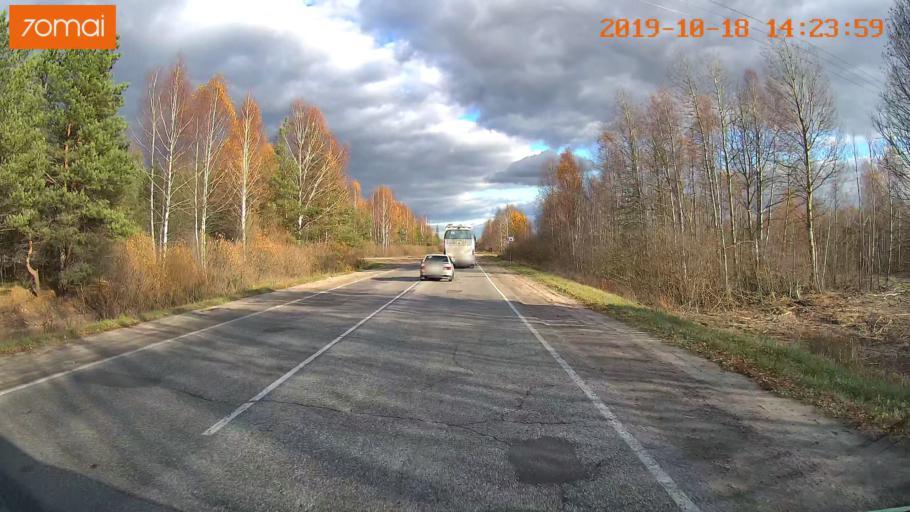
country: RU
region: Rjazan
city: Tuma
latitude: 55.1475
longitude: 40.4925
